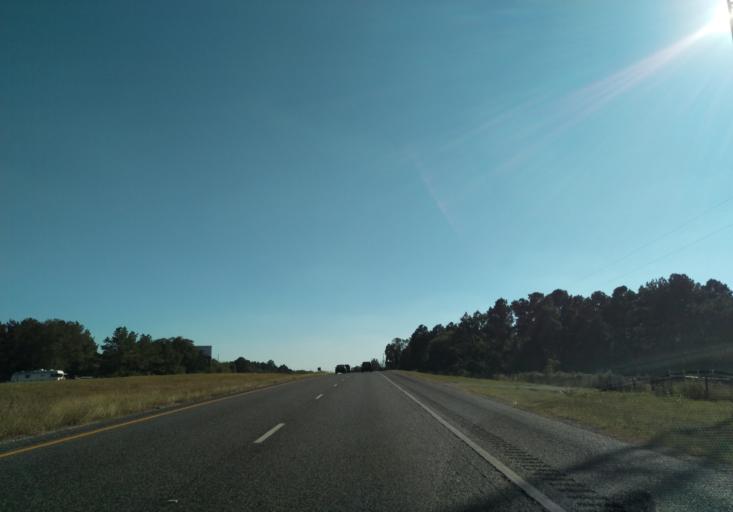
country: US
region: Texas
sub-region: Waller County
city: Hempstead
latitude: 30.1723
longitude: -96.0660
